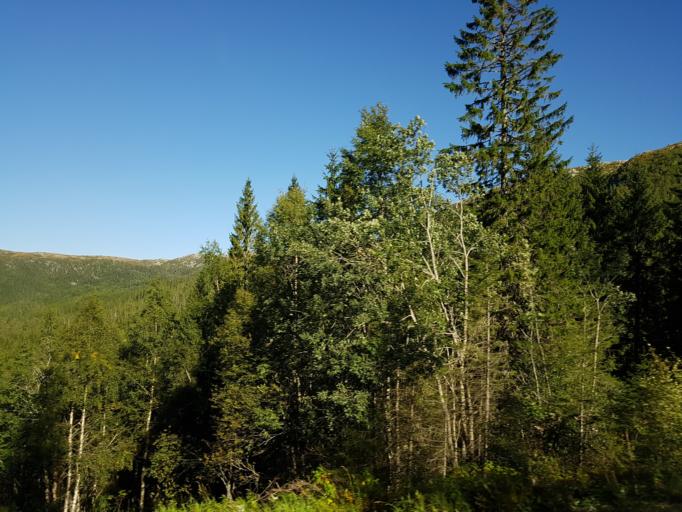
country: NO
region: Sor-Trondelag
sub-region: Afjord
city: A i Afjord
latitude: 63.7183
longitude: 10.2335
